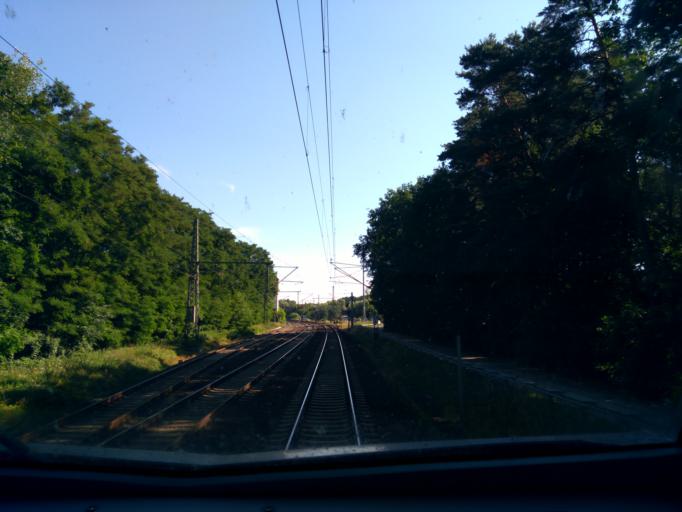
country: DE
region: Brandenburg
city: Bestensee
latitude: 52.2326
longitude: 13.6323
